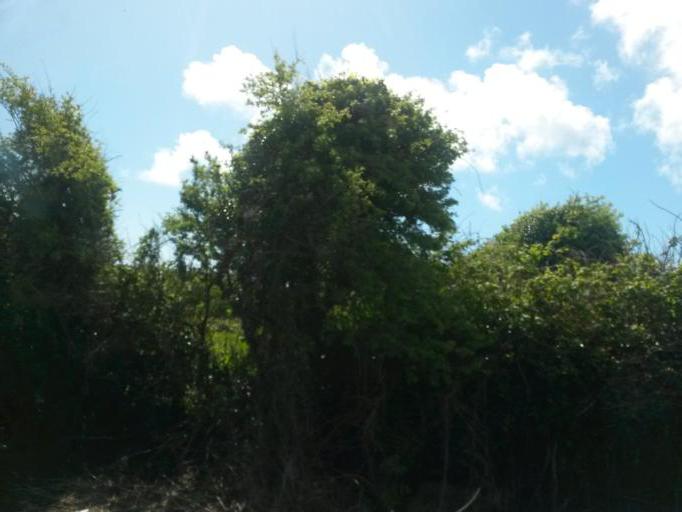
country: IE
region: Munster
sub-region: Waterford
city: Dunmore East
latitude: 52.1791
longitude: -6.8949
